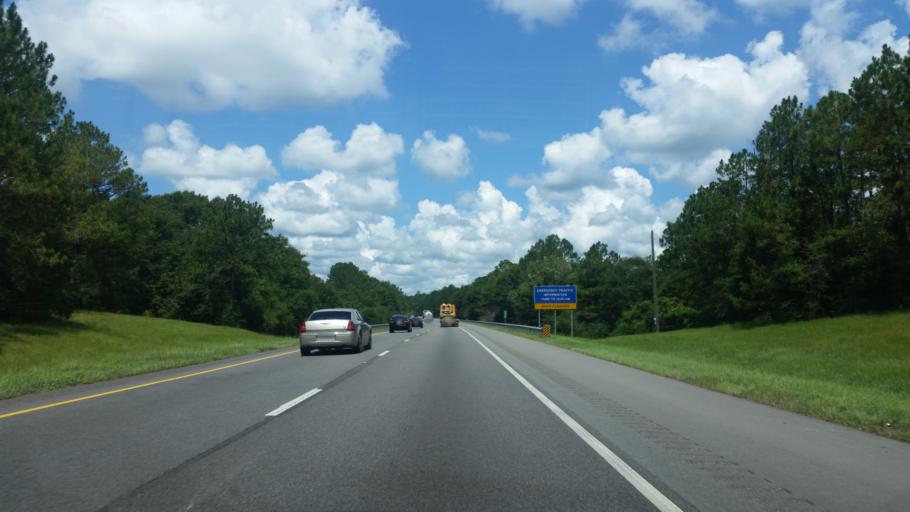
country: US
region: Alabama
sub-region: Baldwin County
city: Robertsdale
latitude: 30.6324
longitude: -87.6324
